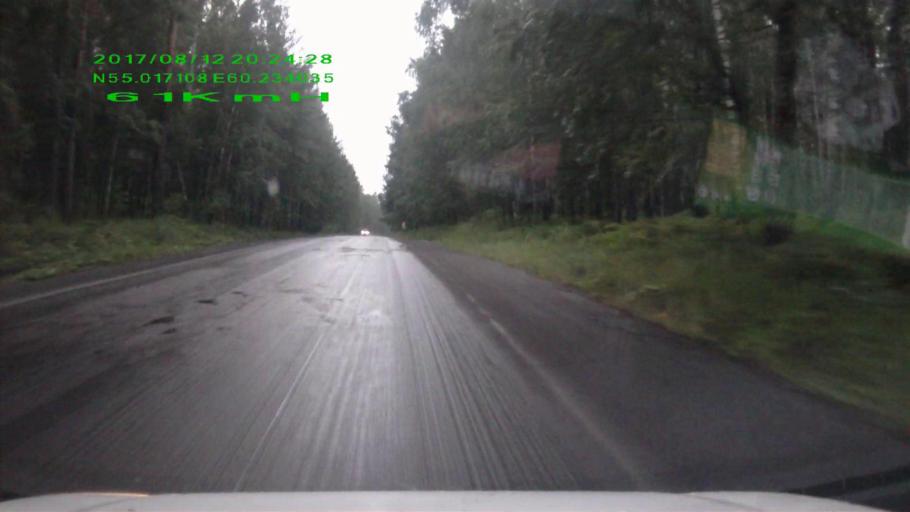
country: RU
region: Chelyabinsk
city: Miass
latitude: 55.0169
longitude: 60.2338
